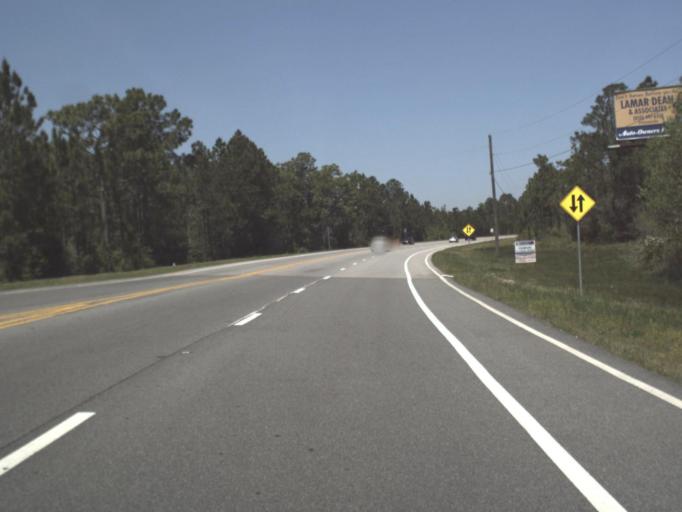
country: US
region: Florida
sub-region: Escambia County
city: Myrtle Grove
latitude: 30.3637
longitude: -87.3600
